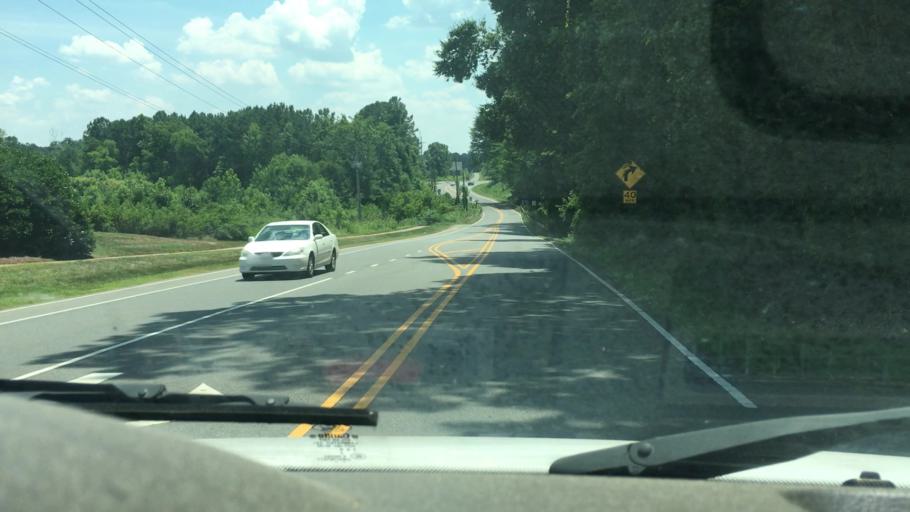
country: US
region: North Carolina
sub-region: Mecklenburg County
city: Huntersville
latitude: 35.4025
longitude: -80.8696
